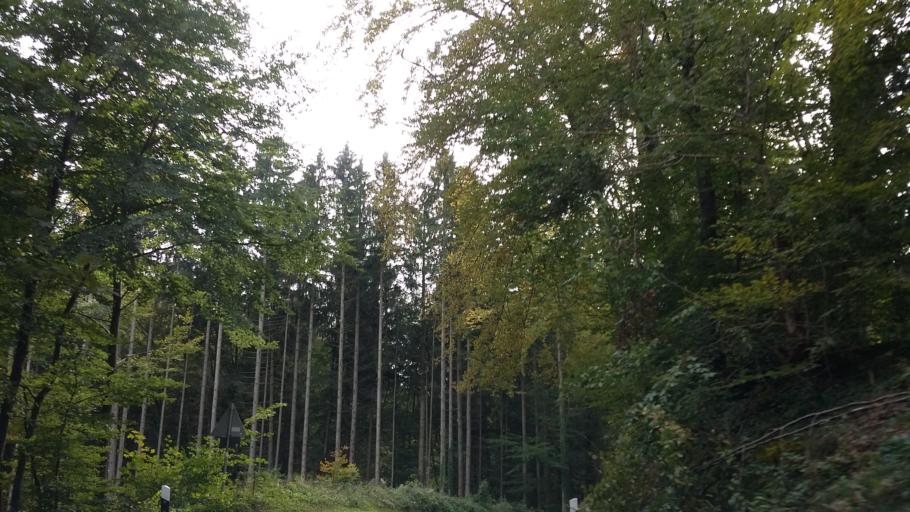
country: DE
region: Bavaria
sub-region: Upper Bavaria
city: Munsing
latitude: 47.8755
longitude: 11.3401
